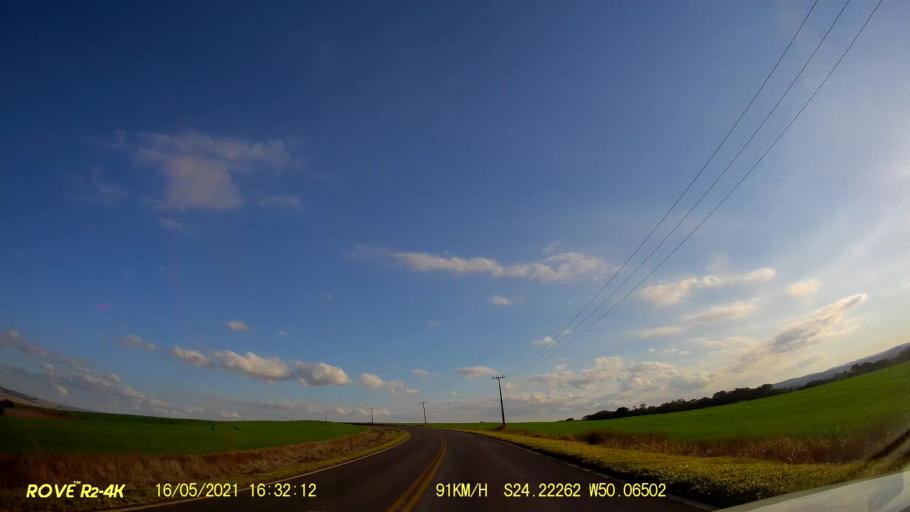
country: BR
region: Parana
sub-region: Pirai Do Sul
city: Pirai do Sul
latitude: -24.2233
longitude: -50.0652
